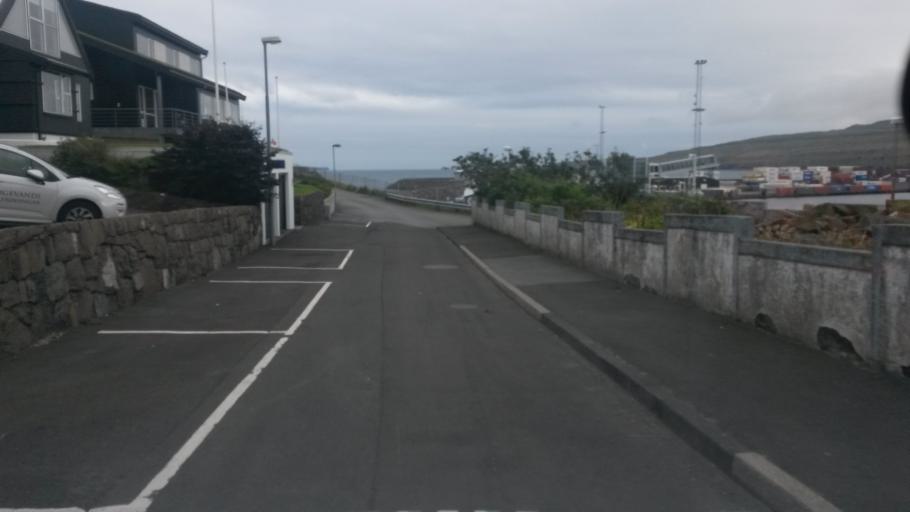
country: FO
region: Streymoy
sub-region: Torshavn
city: Torshavn
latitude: 62.0092
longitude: -6.7668
